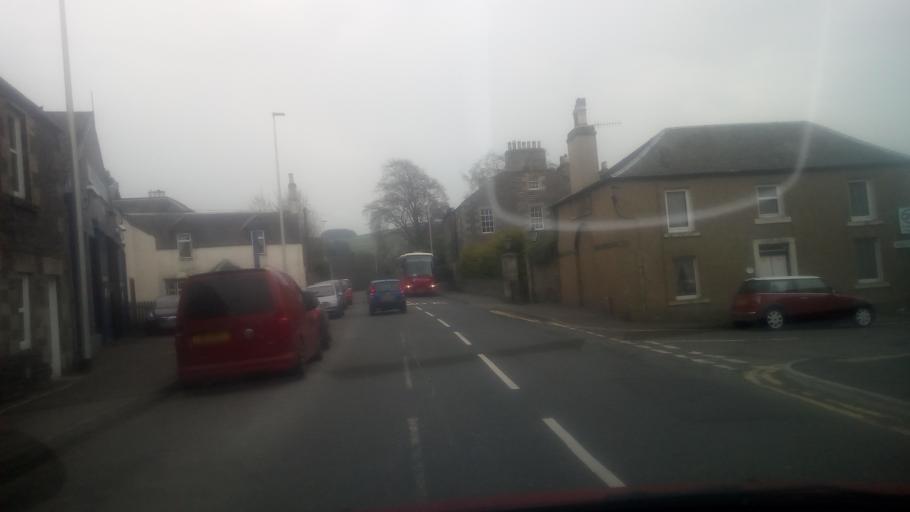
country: GB
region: Scotland
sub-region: The Scottish Borders
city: Galashiels
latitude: 55.6956
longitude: -2.8644
